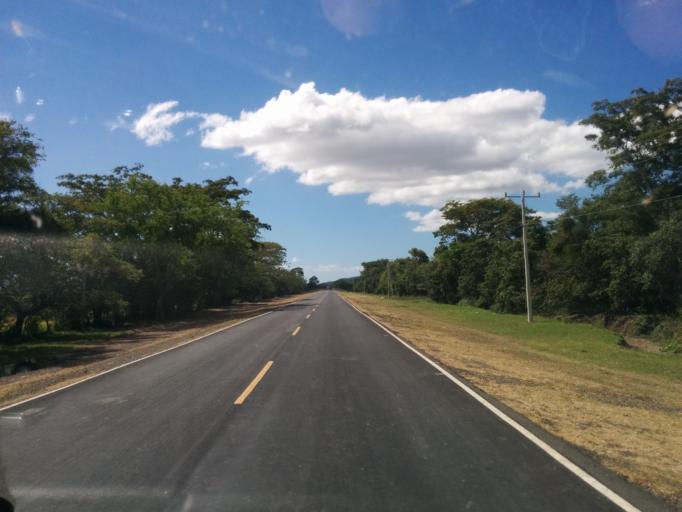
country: NI
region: Matagalpa
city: Ciudad Dario
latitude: 12.8778
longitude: -86.1901
